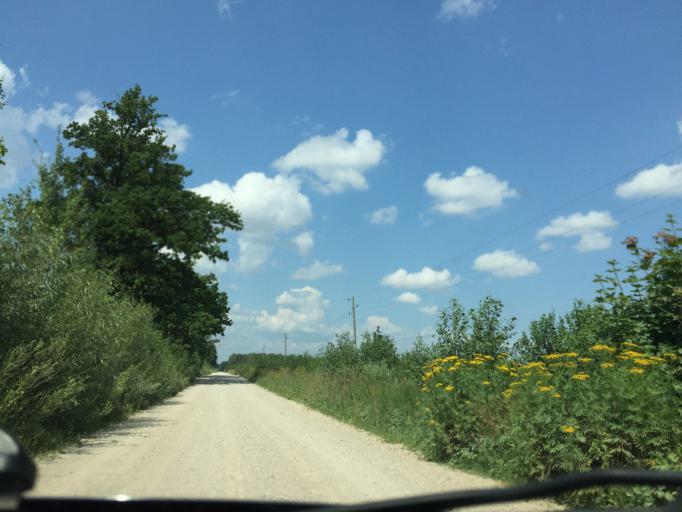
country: LT
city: Zagare
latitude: 56.3817
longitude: 23.2732
